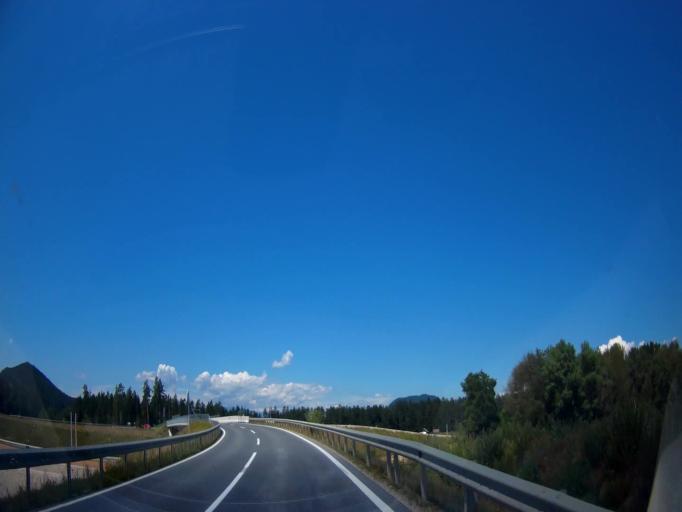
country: AT
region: Carinthia
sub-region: Politischer Bezirk Volkermarkt
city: Bleiburg/Pliberk
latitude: 46.6085
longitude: 14.7832
